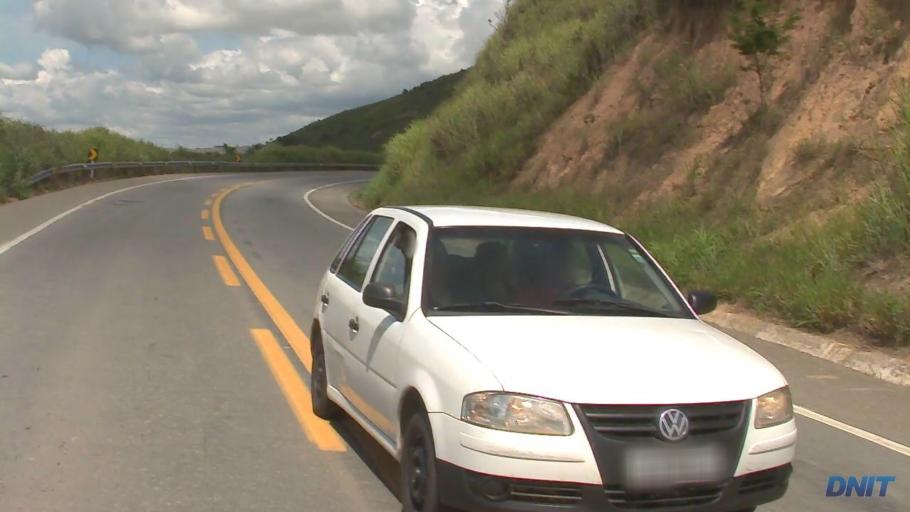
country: BR
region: Minas Gerais
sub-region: Governador Valadares
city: Governador Valadares
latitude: -18.9736
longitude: -42.0958
